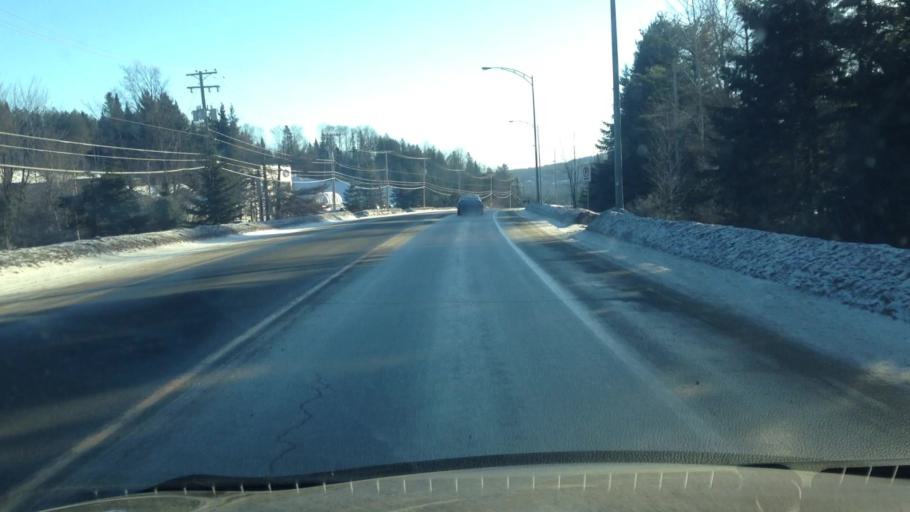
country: CA
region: Quebec
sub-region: Laurentides
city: Saint-Sauveur
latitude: 45.9071
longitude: -74.2532
